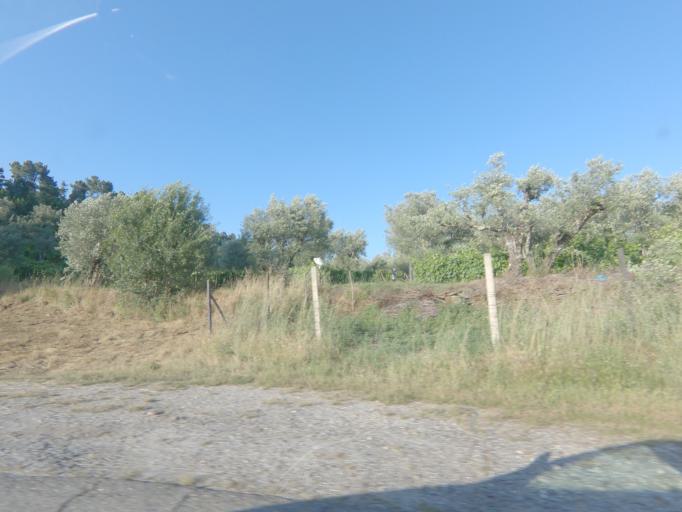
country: PT
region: Vila Real
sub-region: Vila Real
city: Vila Real
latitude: 41.2747
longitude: -7.6690
